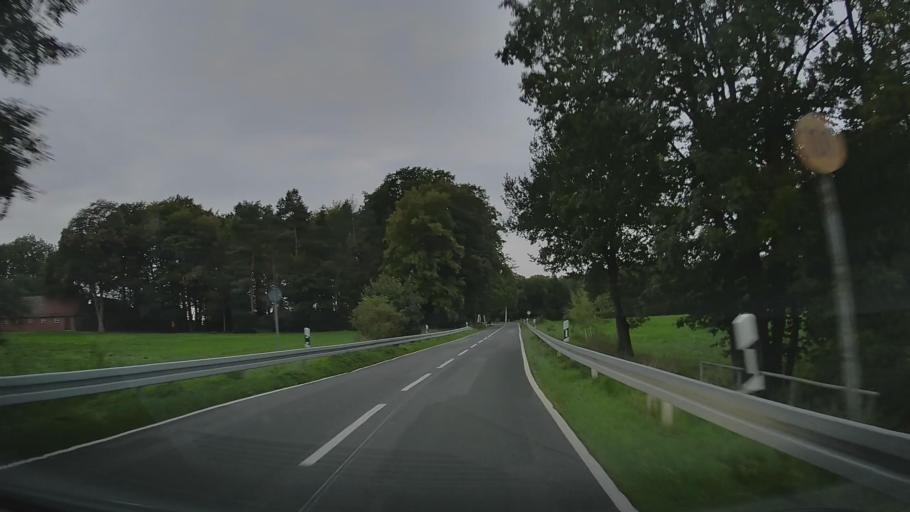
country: DE
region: Lower Saxony
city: Dunsen
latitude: 52.8930
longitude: 8.6636
